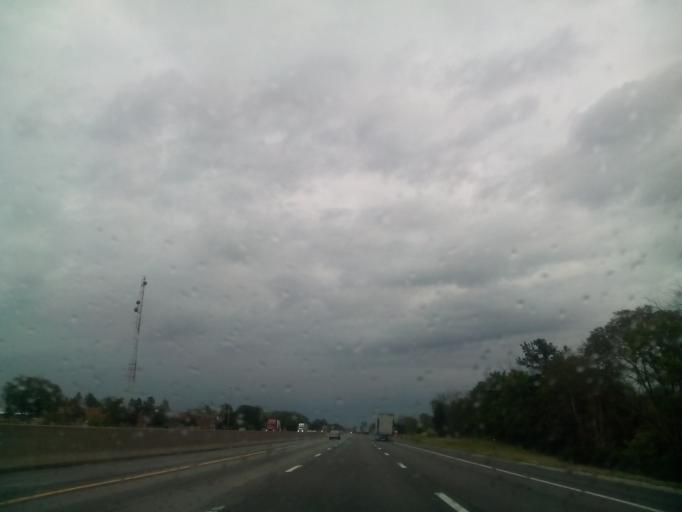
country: US
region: Ohio
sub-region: Ottawa County
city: Elmore
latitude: 41.4713
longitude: -83.3242
